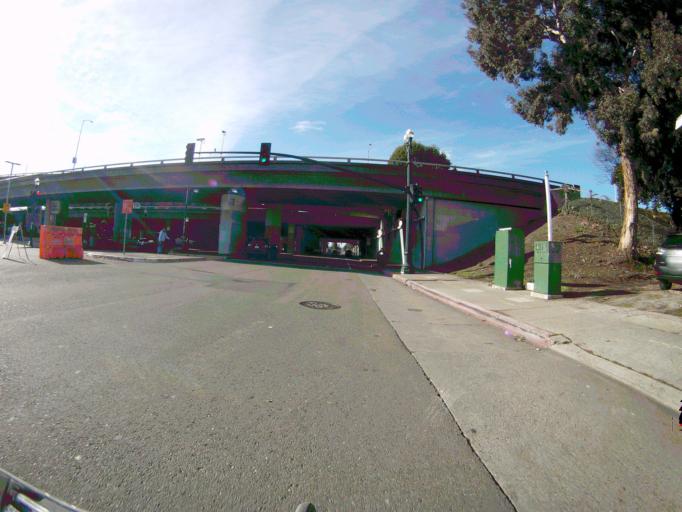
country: US
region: California
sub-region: Alameda County
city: Emeryville
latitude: 37.8295
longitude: -122.2661
